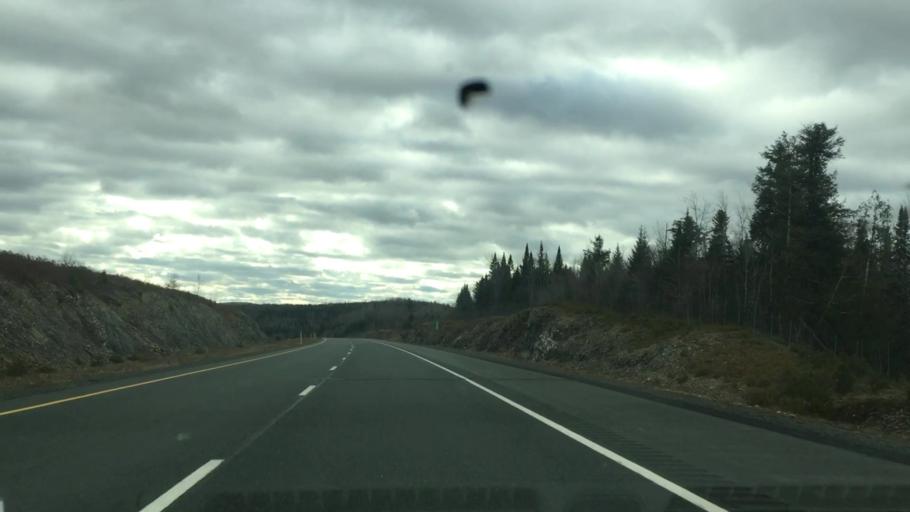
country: US
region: Maine
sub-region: Aroostook County
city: Easton
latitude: 46.6038
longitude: -67.7446
